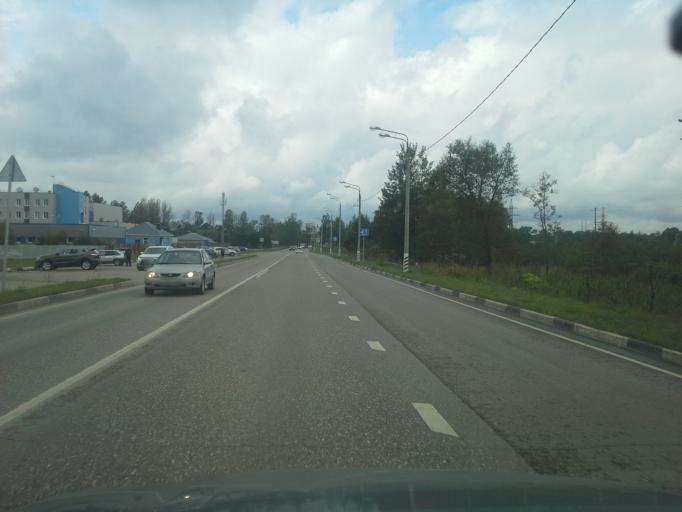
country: RU
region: Moskovskaya
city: Ruza
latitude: 55.7092
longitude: 36.1917
